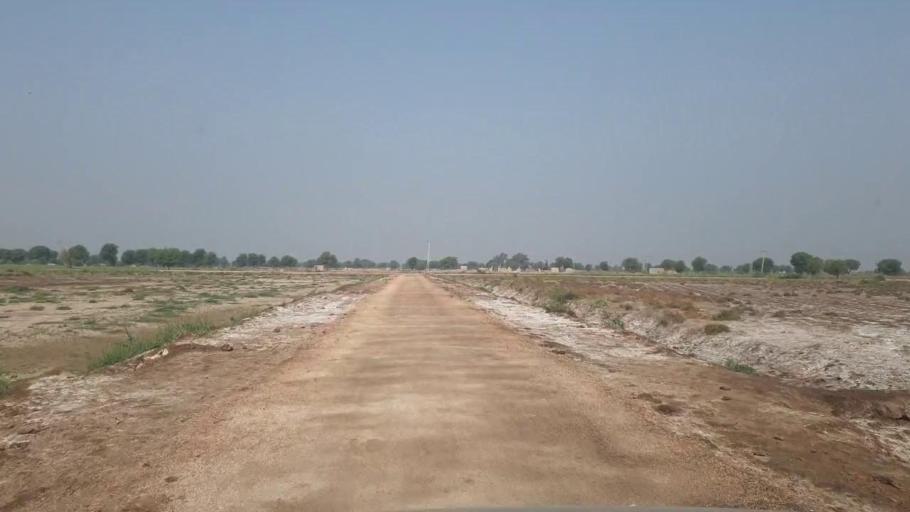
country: PK
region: Sindh
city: Umarkot
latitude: 25.4163
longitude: 69.6779
